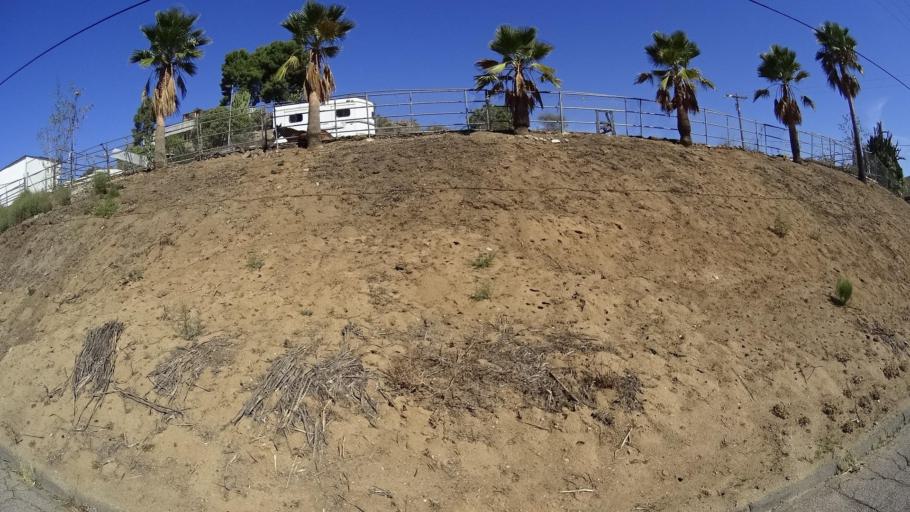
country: US
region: California
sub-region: San Diego County
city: Harbison Canyon
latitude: 32.8669
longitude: -116.8543
